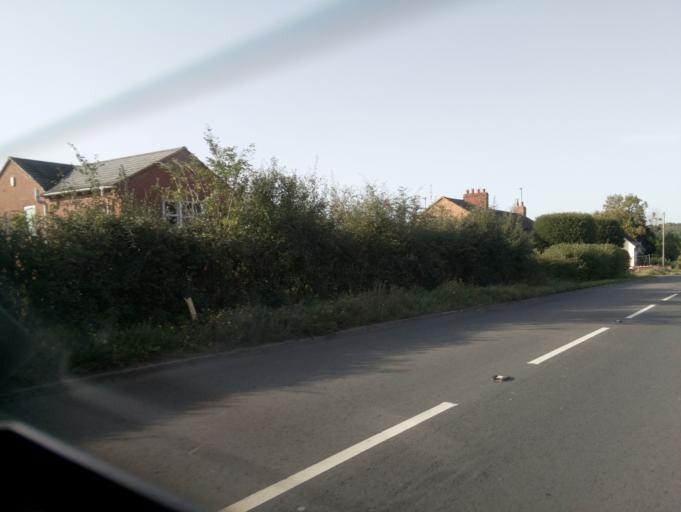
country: GB
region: England
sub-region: Gloucestershire
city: Gloucester
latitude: 51.9246
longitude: -2.2934
